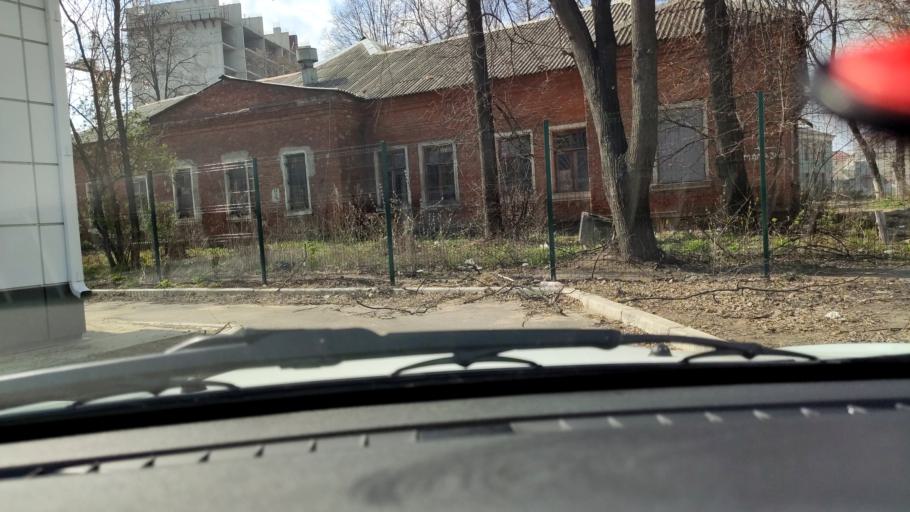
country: RU
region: Voronezj
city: Voronezh
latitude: 51.6979
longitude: 39.1982
